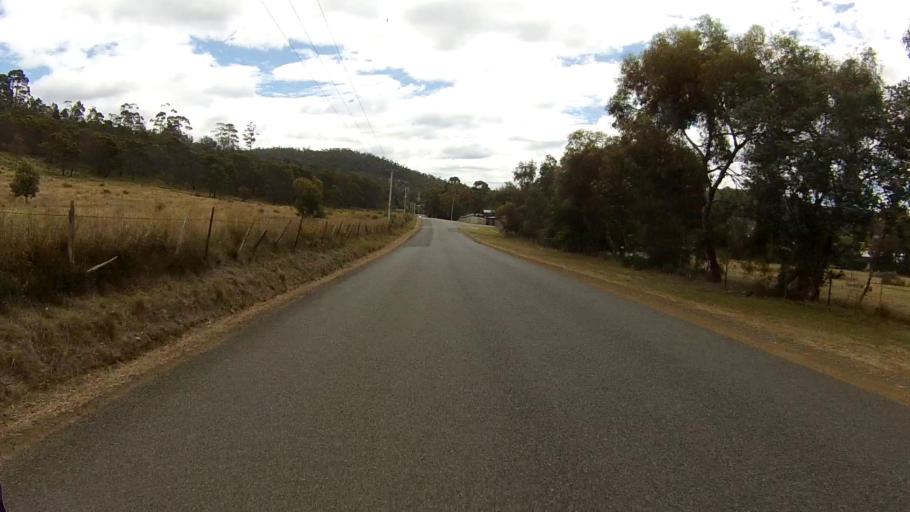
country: AU
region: Tasmania
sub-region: Sorell
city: Sorell
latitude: -42.5709
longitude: 147.8841
